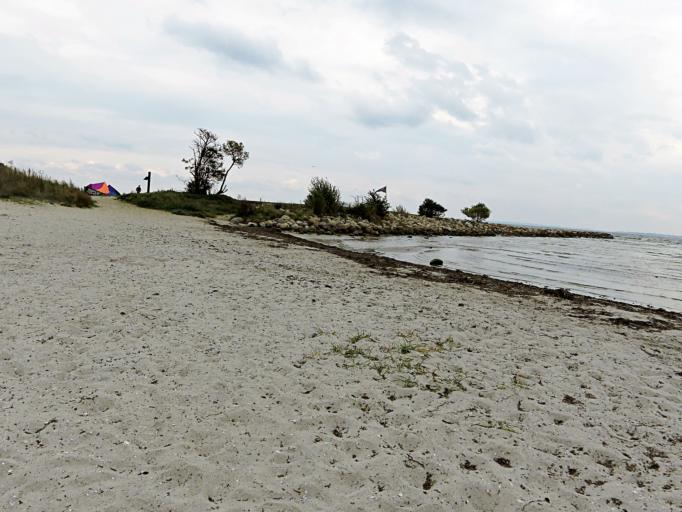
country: DK
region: Capital Region
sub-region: Fredensborg Kommune
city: Niva
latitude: 55.9376
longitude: 12.5276
